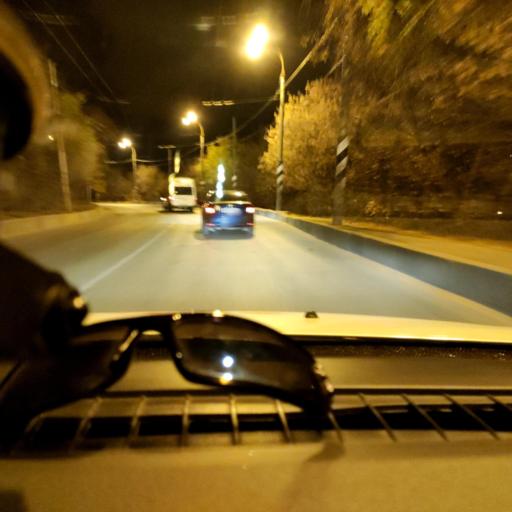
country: RU
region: Samara
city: Samara
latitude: 53.1521
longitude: 50.0923
